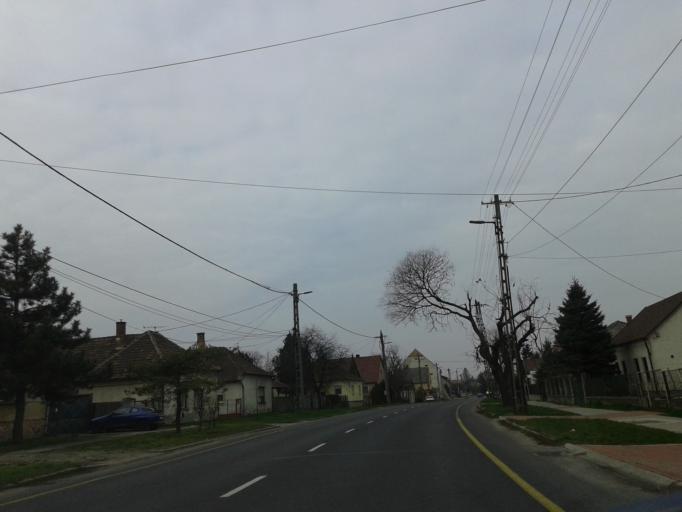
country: HU
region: Komarom-Esztergom
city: Komarom
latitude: 47.7347
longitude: 18.1785
